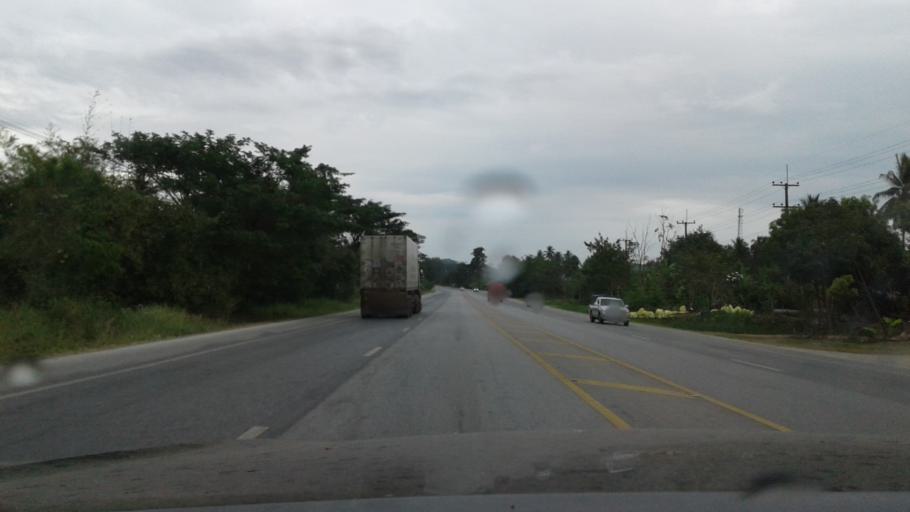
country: TH
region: Changwat Udon Thani
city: Nong Wua So
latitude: 17.2454
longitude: 102.5490
